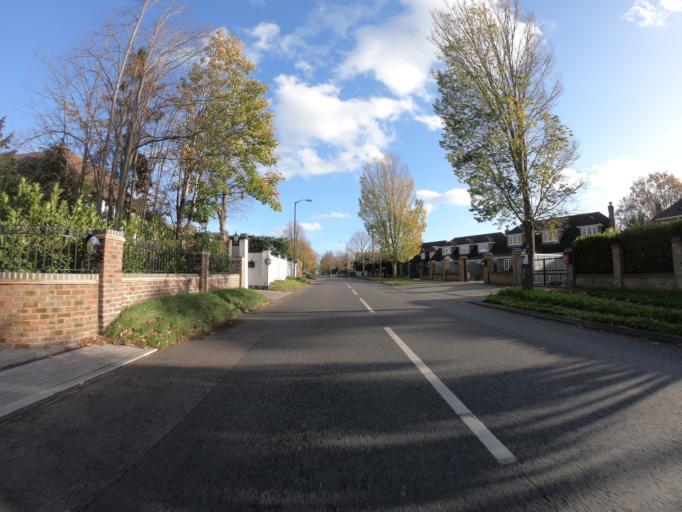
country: GB
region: England
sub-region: Greater London
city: Orpington
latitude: 51.3993
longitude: 0.0956
